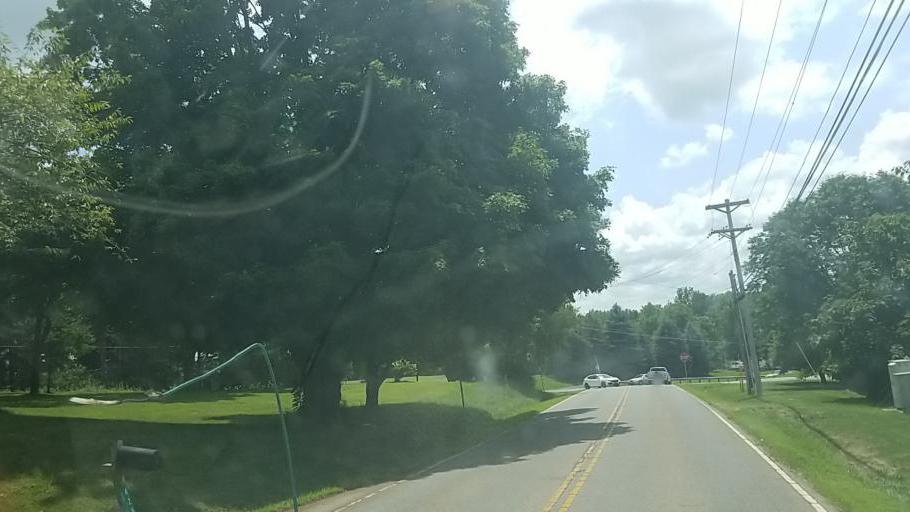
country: US
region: Ohio
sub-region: Fairfield County
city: Pickerington
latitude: 39.8919
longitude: -82.7487
